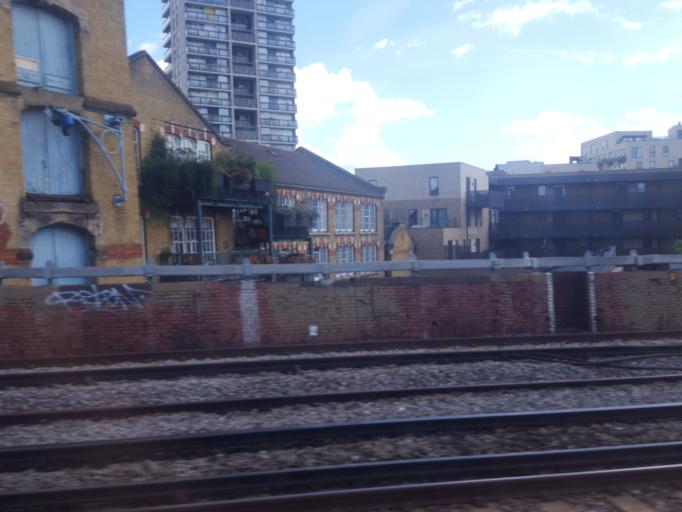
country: GB
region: England
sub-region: Greater London
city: City of London
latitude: 51.4978
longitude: -0.0720
